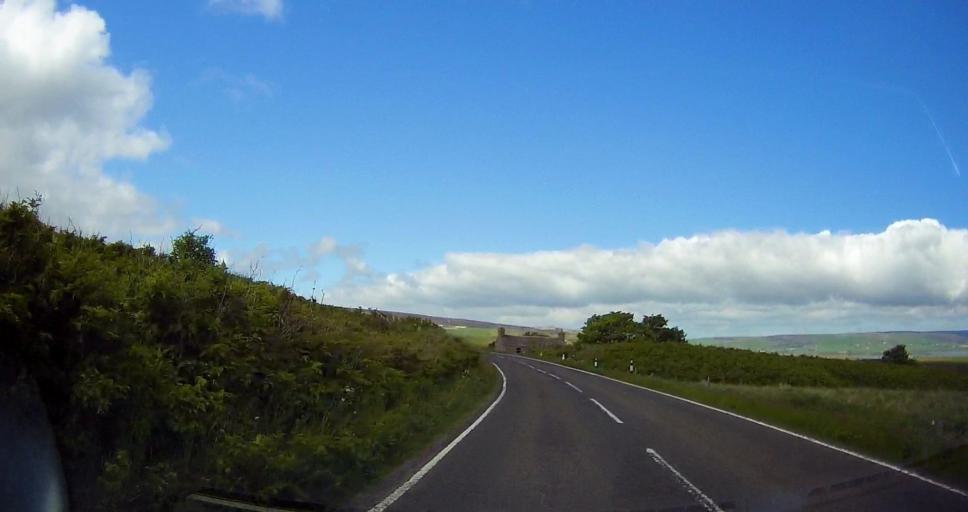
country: GB
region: Scotland
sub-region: Orkney Islands
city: Orkney
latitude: 58.9881
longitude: -3.0544
